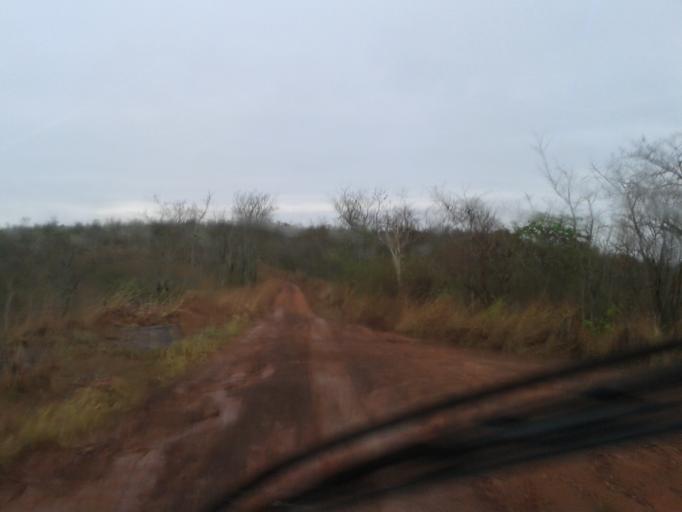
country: BR
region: Minas Gerais
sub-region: Campina Verde
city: Campina Verde
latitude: -19.3325
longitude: -49.5172
